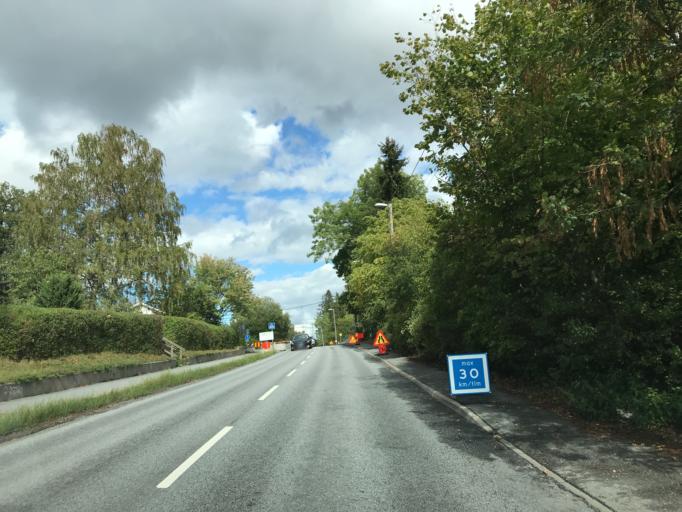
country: SE
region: Stockholm
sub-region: Sollentuna Kommun
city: Sollentuna
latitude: 59.4503
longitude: 17.9526
